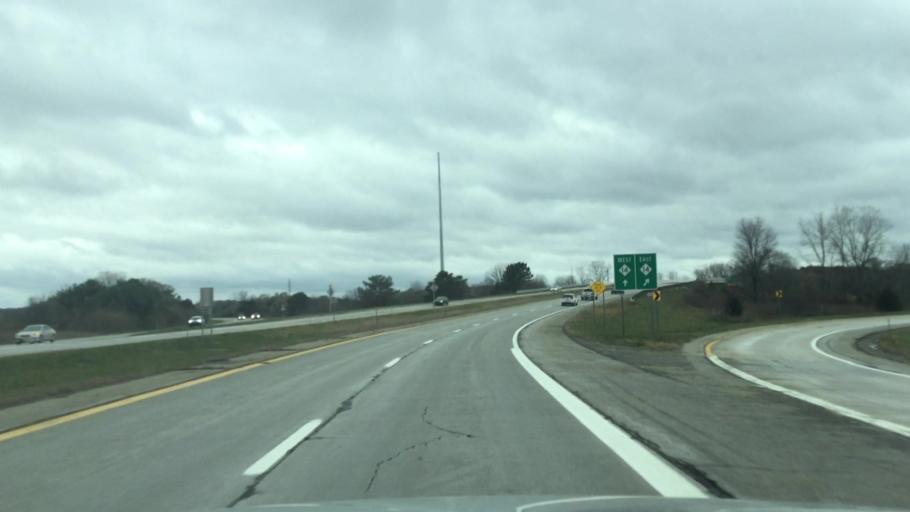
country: US
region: Michigan
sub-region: Washtenaw County
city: Ypsilanti
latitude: 42.3256
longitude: -83.6288
